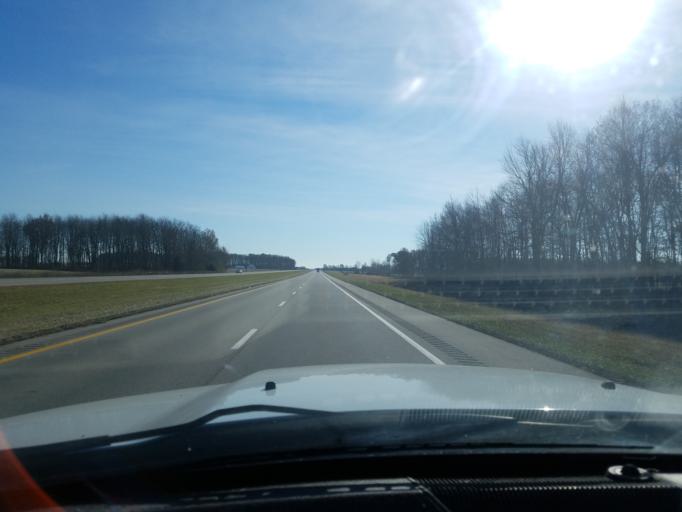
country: US
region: Ohio
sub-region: Adams County
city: Winchester
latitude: 38.9994
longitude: -83.7758
